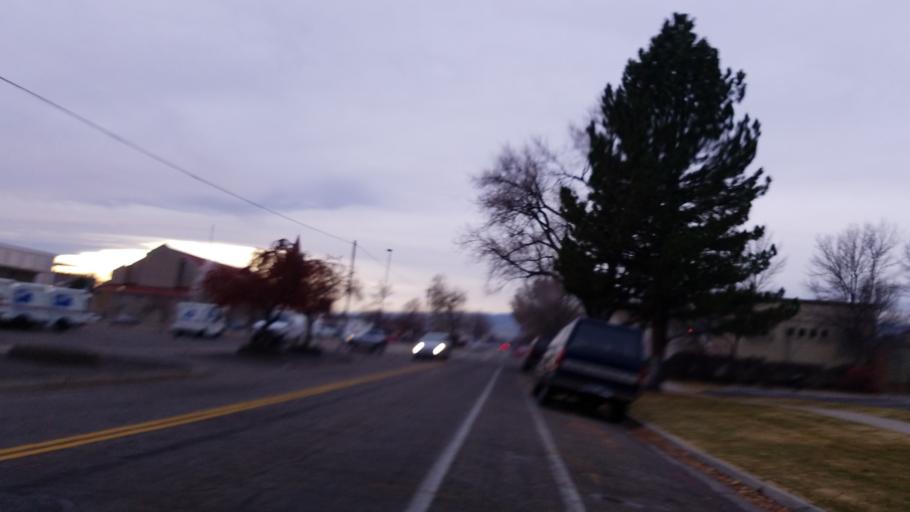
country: US
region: Colorado
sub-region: Mesa County
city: Grand Junction
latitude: 39.0710
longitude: -108.5679
